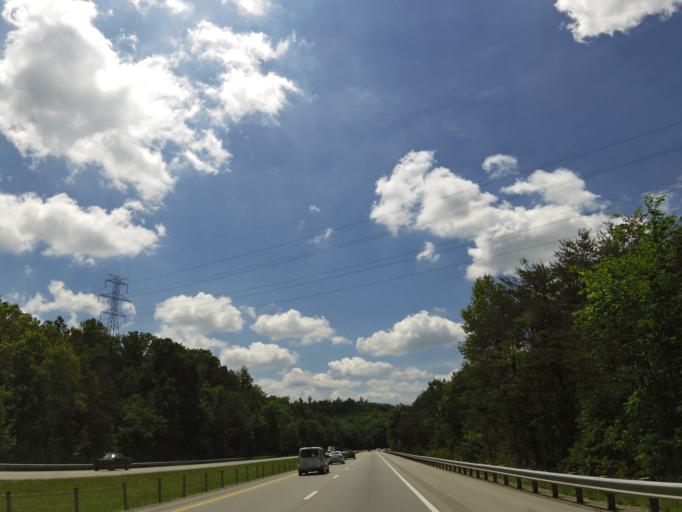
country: US
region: Kentucky
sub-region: Whitley County
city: Corbin
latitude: 36.8737
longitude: -84.1488
